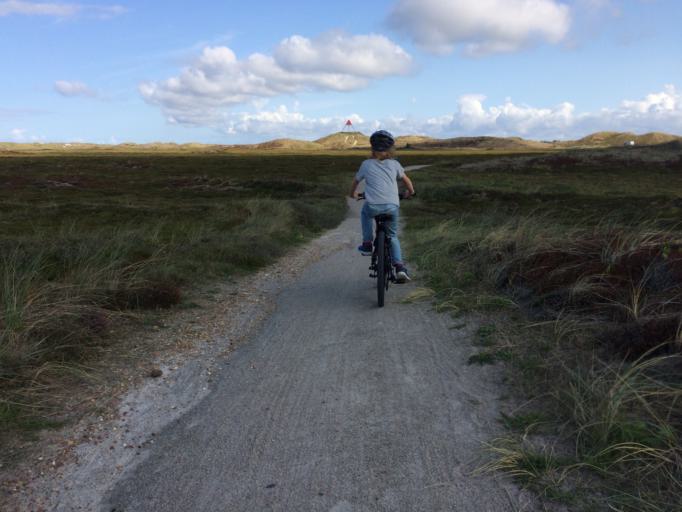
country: DK
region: Central Jutland
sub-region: Ringkobing-Skjern Kommune
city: Hvide Sande
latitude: 55.9131
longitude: 8.1601
